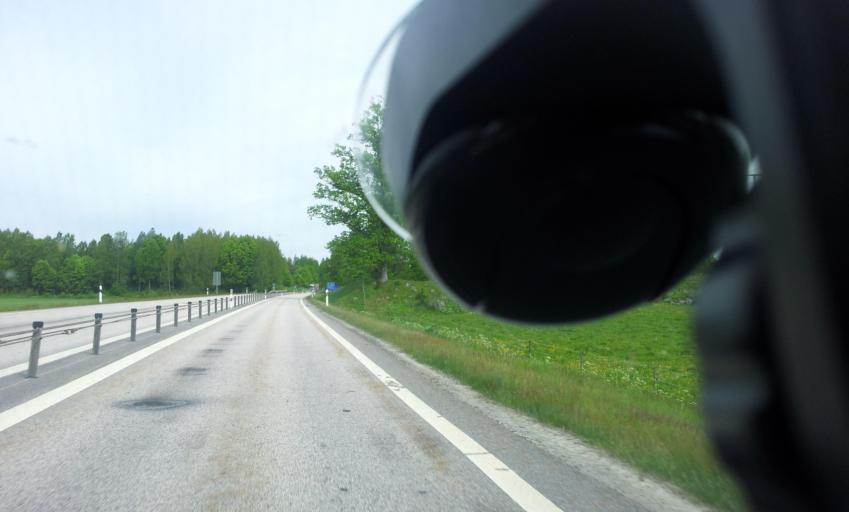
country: SE
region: Kalmar
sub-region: Vasterviks Kommun
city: Forserum
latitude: 58.0719
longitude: 16.5192
